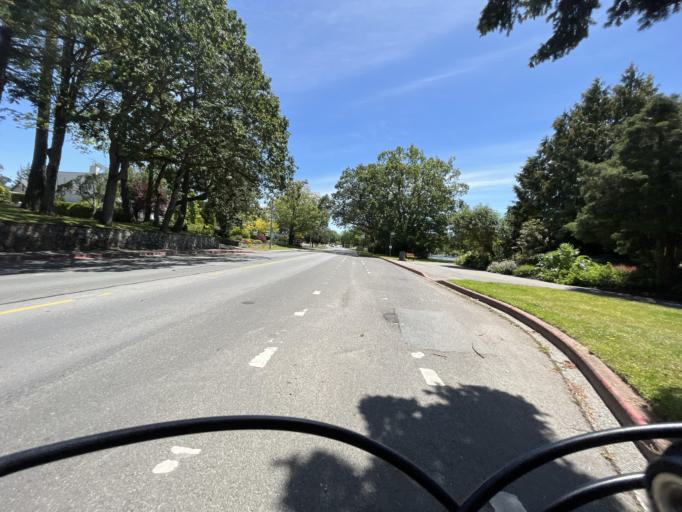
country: CA
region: British Columbia
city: Victoria
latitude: 48.4524
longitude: -123.4179
